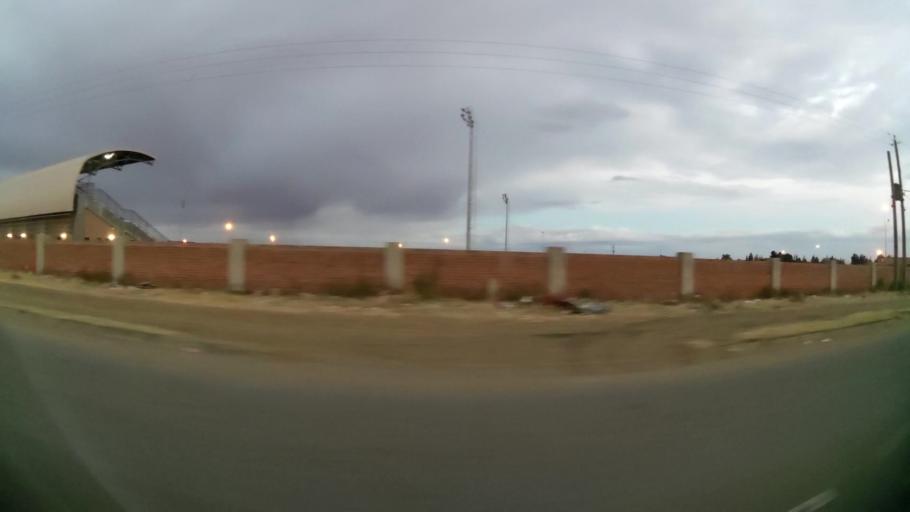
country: ZA
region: Orange Free State
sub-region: Lejweleputswa District Municipality
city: Welkom
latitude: -27.9588
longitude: 26.7856
